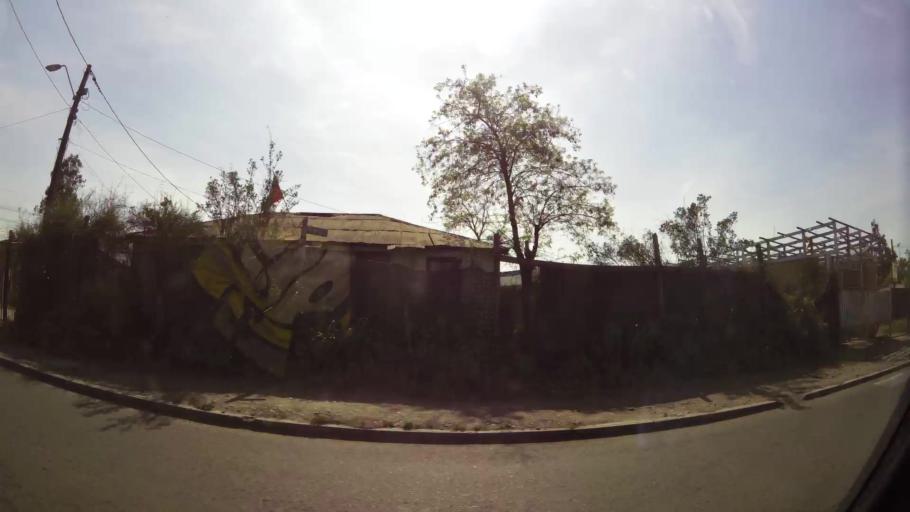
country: CL
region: Santiago Metropolitan
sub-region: Provincia de Santiago
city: Lo Prado
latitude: -33.4262
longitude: -70.7660
